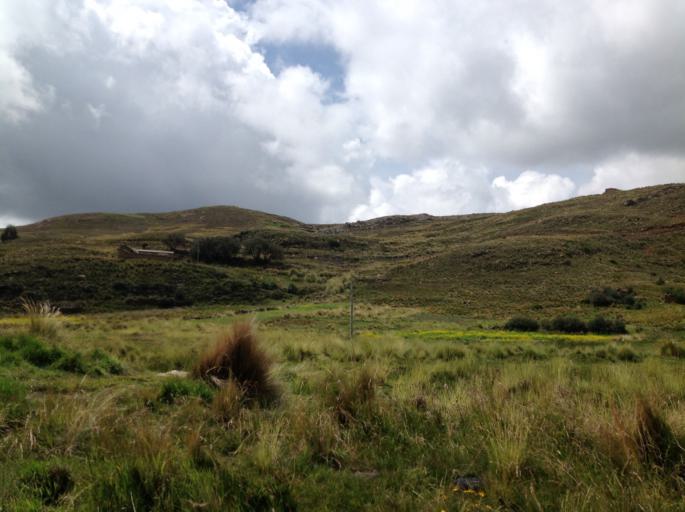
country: BO
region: La Paz
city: Yumani
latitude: -15.7714
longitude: -68.9970
